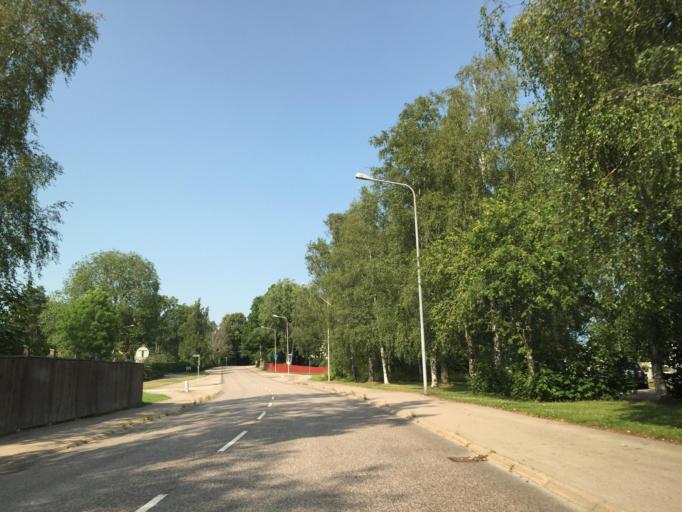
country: SE
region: Vaestra Goetaland
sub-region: Vanersborgs Kommun
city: Vanersborg
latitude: 58.3715
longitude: 12.2862
